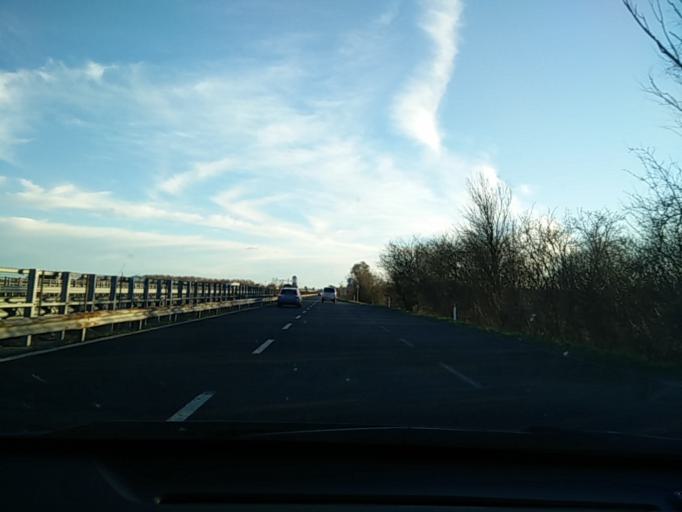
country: IT
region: Friuli Venezia Giulia
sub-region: Provincia di Udine
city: Colugna
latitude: 46.1018
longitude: 13.2000
